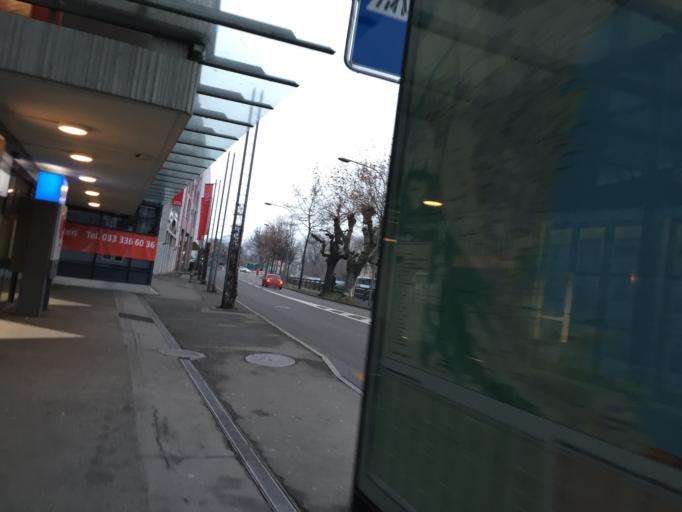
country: CH
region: Bern
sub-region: Thun District
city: Thun
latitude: 46.7583
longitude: 7.6266
